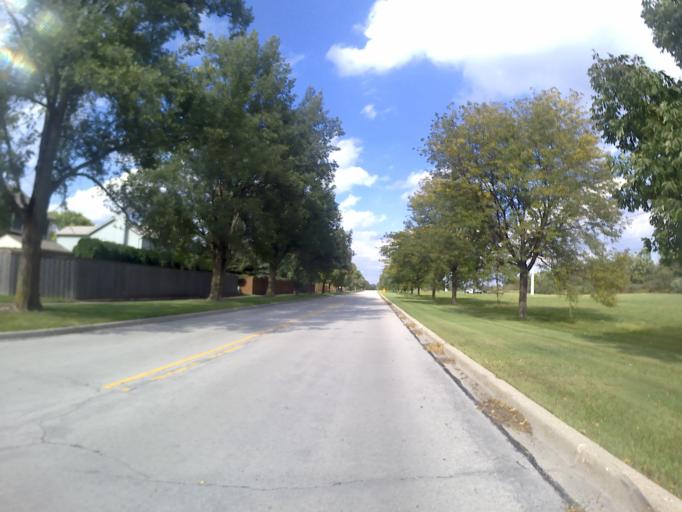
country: US
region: Illinois
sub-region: Will County
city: Bolingbrook
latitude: 41.7283
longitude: -88.0982
